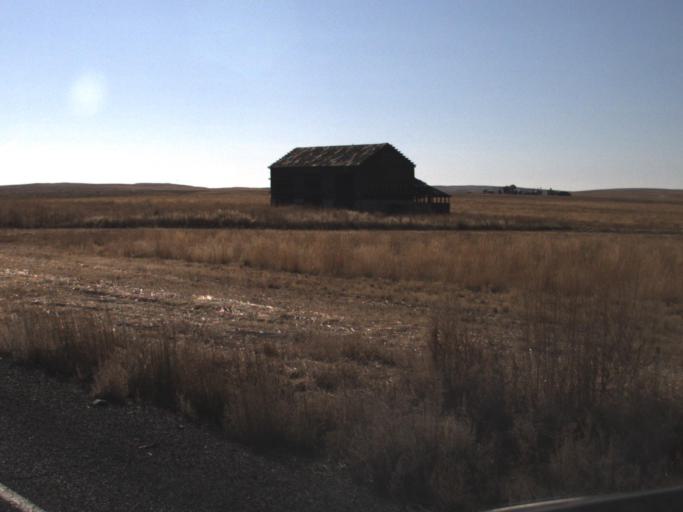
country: US
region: Washington
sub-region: Franklin County
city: Connell
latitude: 46.7369
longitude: -118.5477
